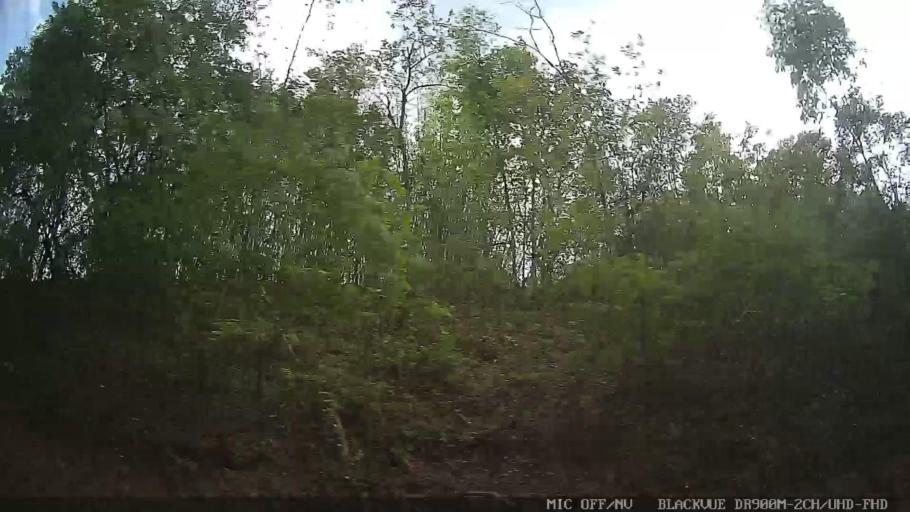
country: BR
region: Sao Paulo
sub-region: Louveira
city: Louveira
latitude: -23.0880
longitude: -46.9374
